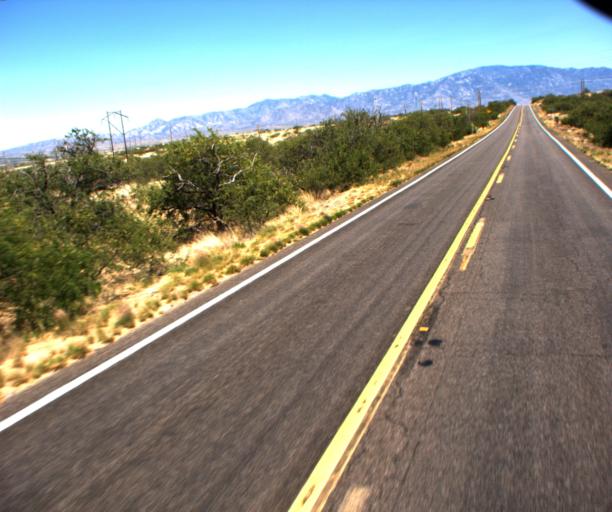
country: US
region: Arizona
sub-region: Pima County
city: Catalina
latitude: 32.6044
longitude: -110.9838
